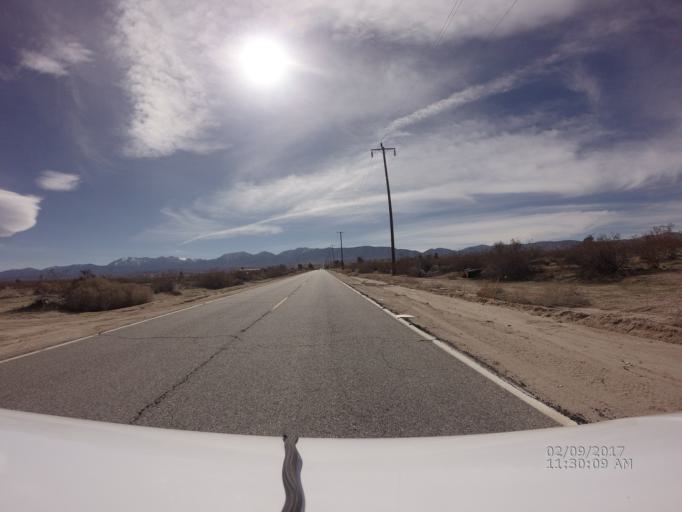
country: US
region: California
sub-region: Los Angeles County
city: Littlerock
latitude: 34.5356
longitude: -117.9229
